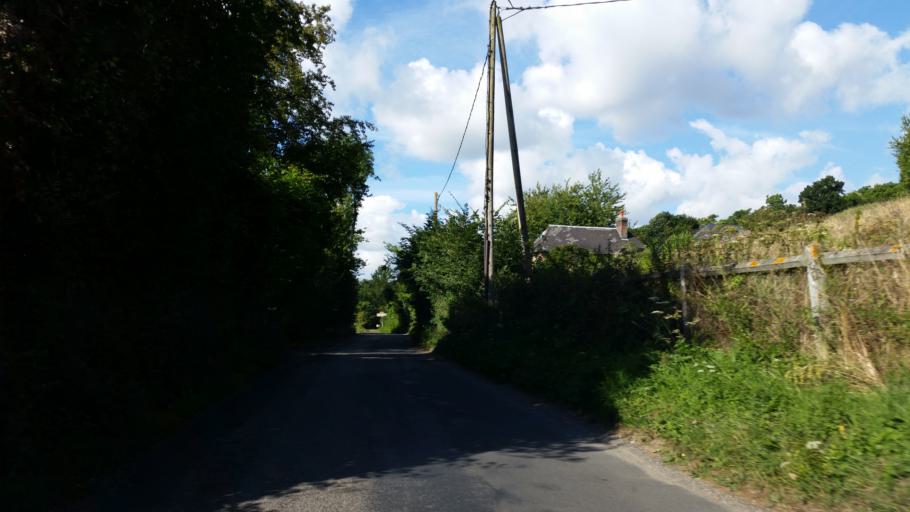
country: FR
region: Lower Normandy
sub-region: Departement du Calvados
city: Equemauville
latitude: 49.3997
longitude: 0.2252
